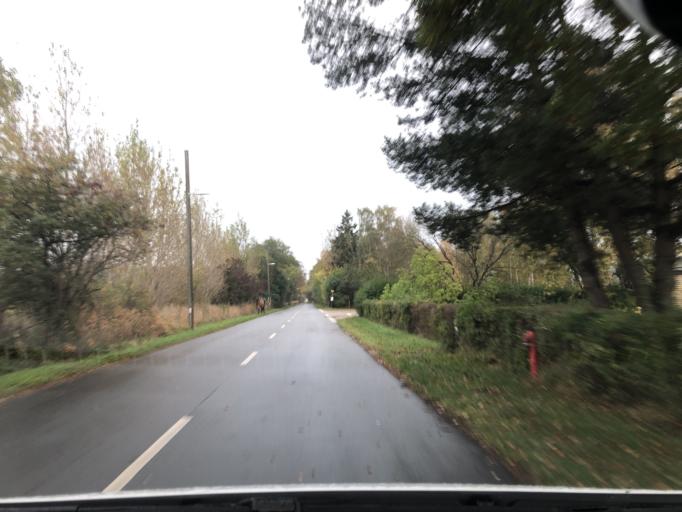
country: DK
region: Capital Region
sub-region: Tarnby Kommune
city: Tarnby
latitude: 55.5651
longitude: 12.5860
